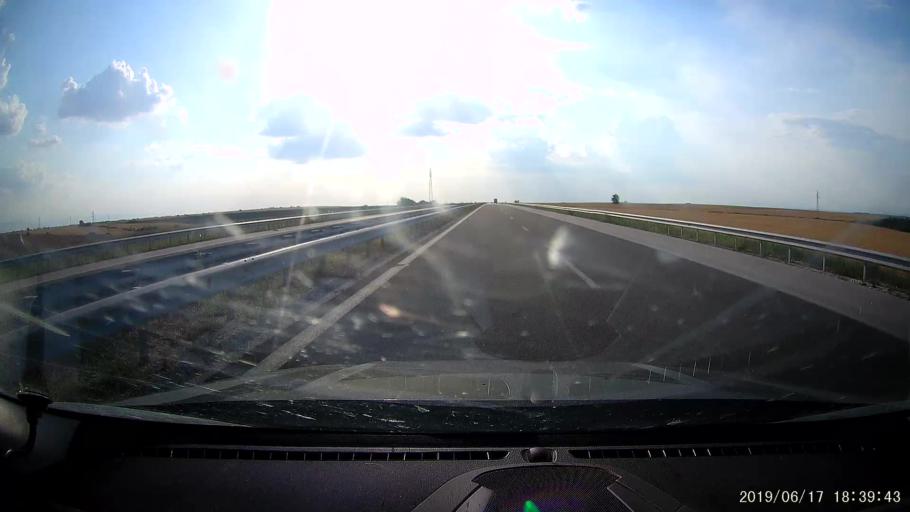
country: BG
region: Stara Zagora
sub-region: Obshtina Chirpan
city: Chirpan
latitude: 42.1479
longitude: 25.2989
